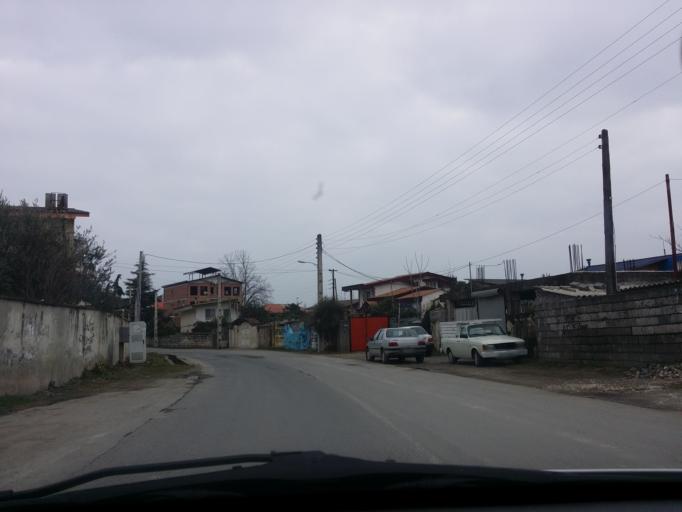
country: IR
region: Mazandaran
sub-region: Nowshahr
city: Nowshahr
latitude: 36.6445
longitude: 51.4812
